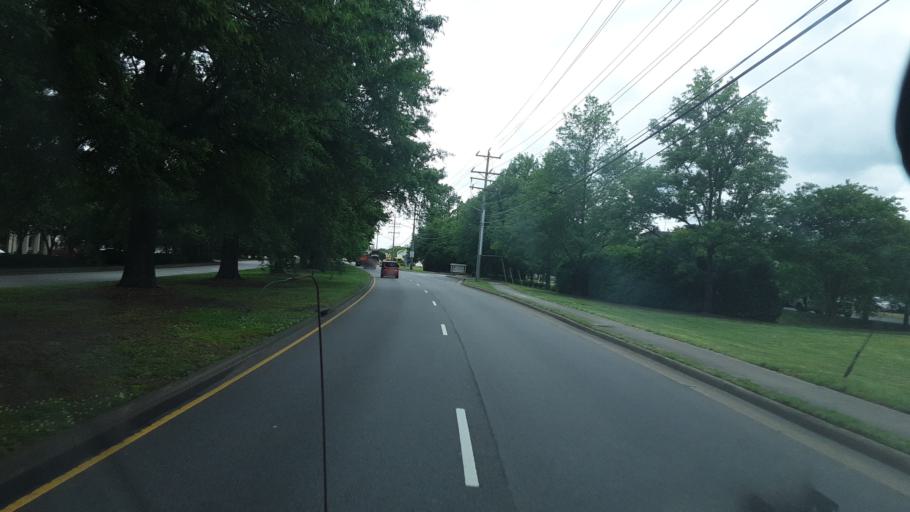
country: US
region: Virginia
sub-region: City of Virginia Beach
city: Virginia Beach
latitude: 36.7714
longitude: -76.0115
